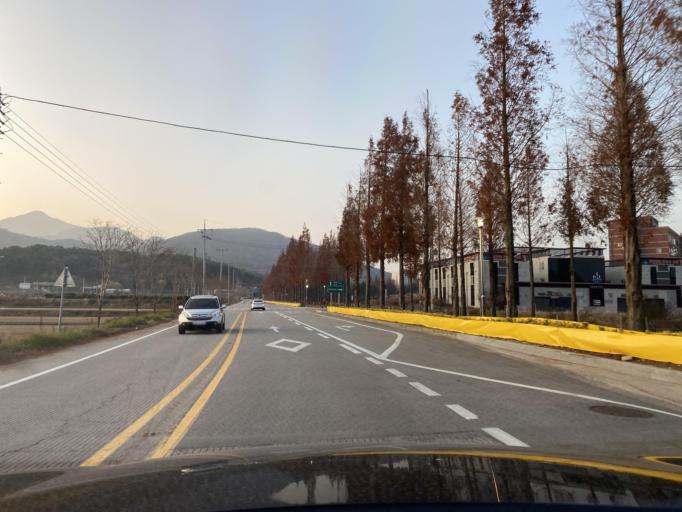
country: KR
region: Chungcheongnam-do
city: Hongsung
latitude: 36.6871
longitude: 126.6596
